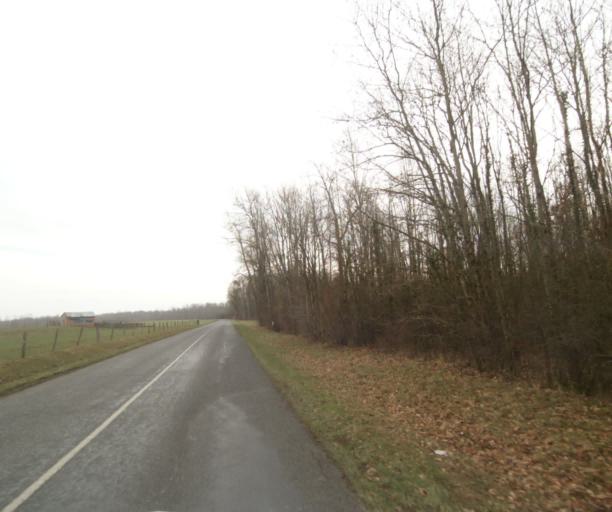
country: FR
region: Champagne-Ardenne
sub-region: Departement de la Marne
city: Pargny-sur-Saulx
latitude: 48.7394
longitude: 4.8543
